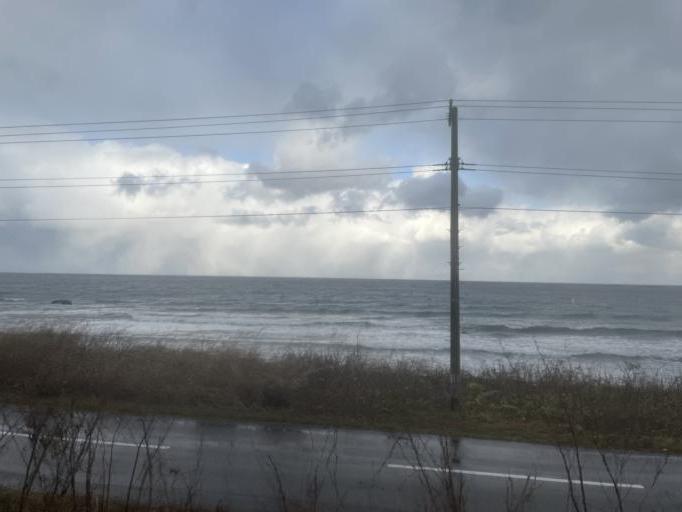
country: JP
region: Aomori
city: Shimokizukuri
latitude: 41.1879
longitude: 140.4566
